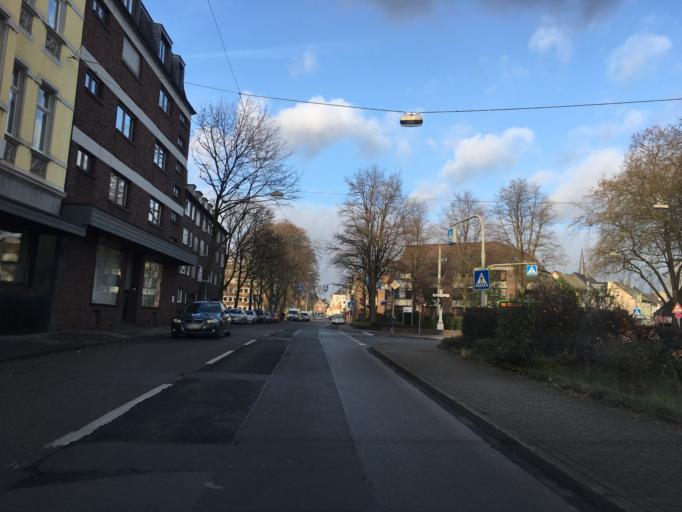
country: DE
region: North Rhine-Westphalia
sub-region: Regierungsbezirk Dusseldorf
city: Oberhausen
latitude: 51.5194
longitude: 6.8464
